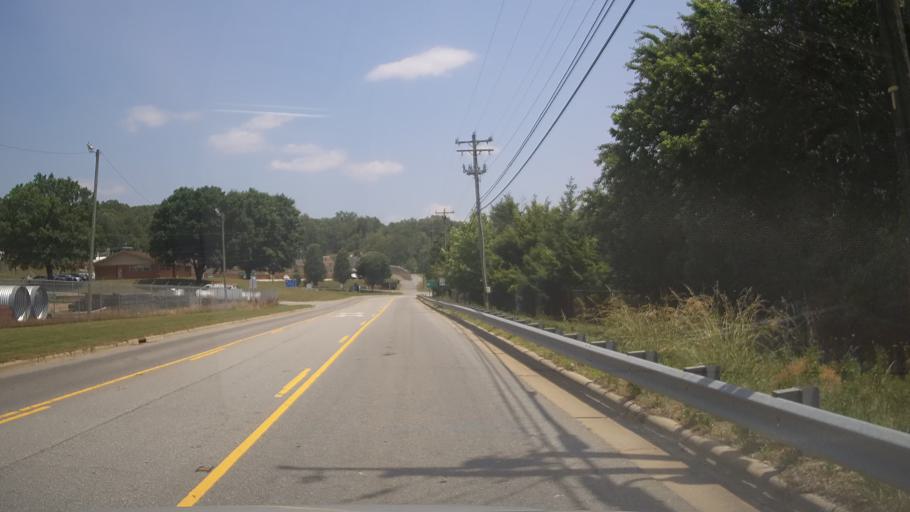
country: US
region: North Carolina
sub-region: McDowell County
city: Marion
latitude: 35.6533
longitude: -81.9570
